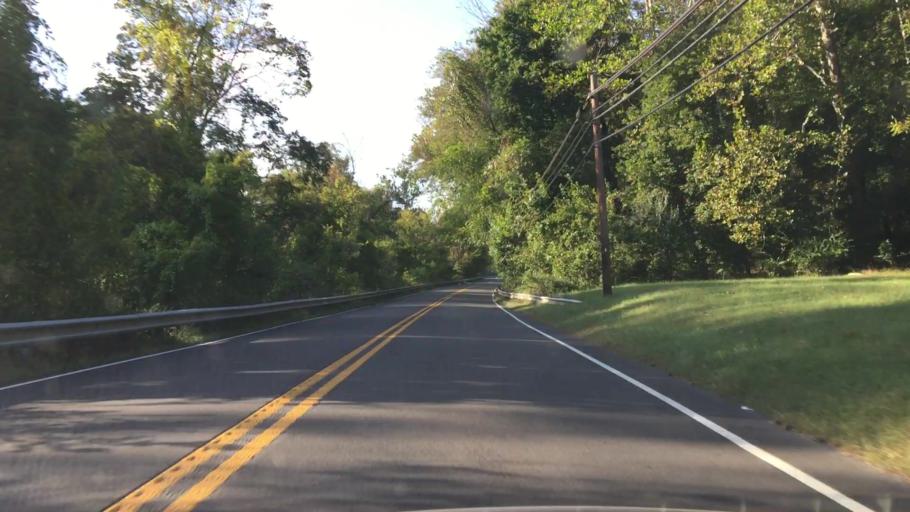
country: US
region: Pennsylvania
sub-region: Bucks County
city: New Hope
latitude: 40.3868
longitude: -74.9571
